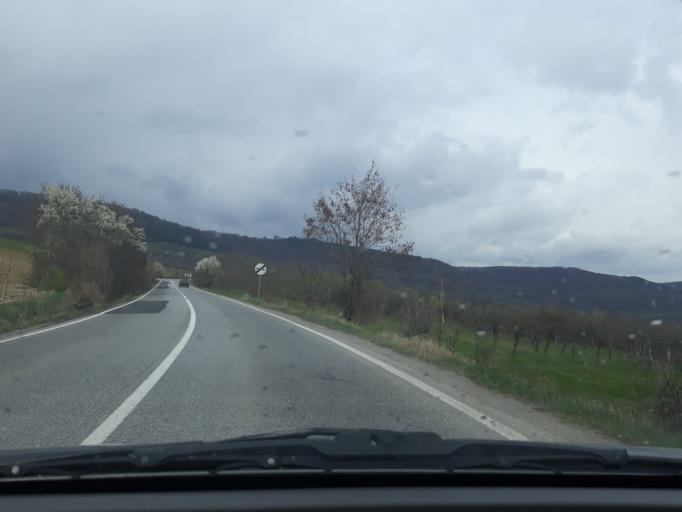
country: RO
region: Harghita
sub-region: Comuna Lupeni
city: Lupeni
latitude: 46.3977
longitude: 25.2155
